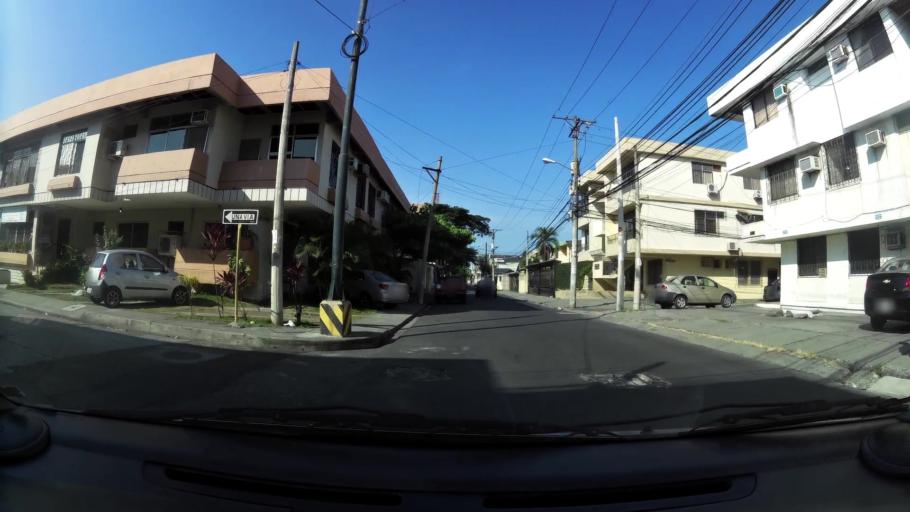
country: EC
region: Guayas
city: Guayaquil
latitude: -2.1735
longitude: -79.9001
